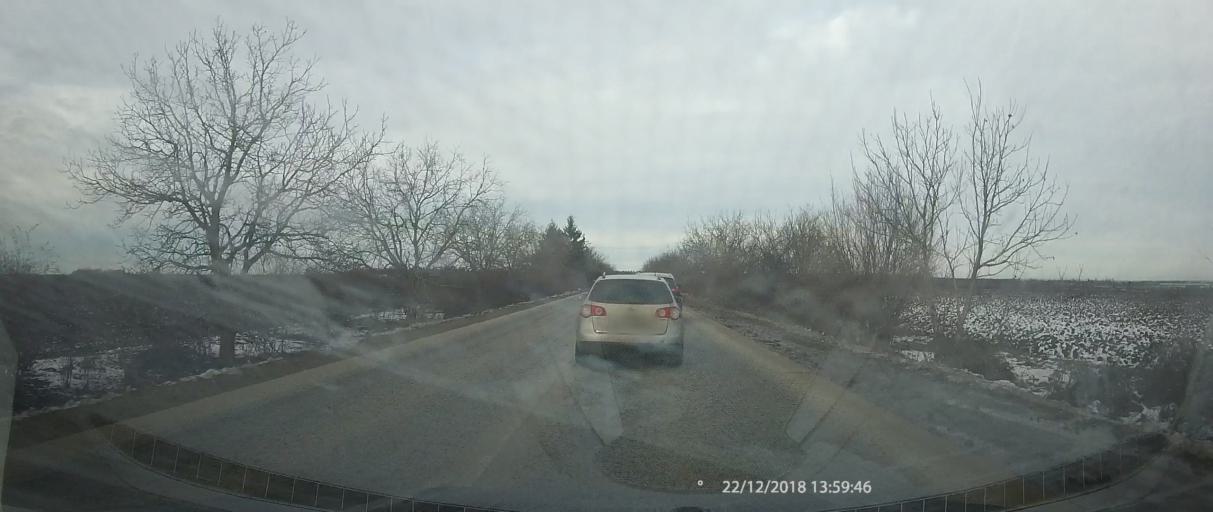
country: BG
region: Pleven
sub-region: Obshtina Dolni Dubnik
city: Dolni Dubnik
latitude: 43.3525
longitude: 24.3436
